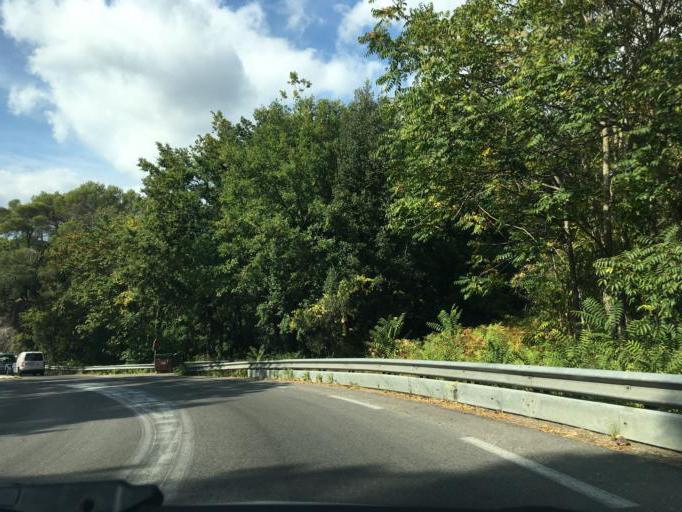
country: FR
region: Provence-Alpes-Cote d'Azur
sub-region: Departement du Var
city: Flayosc
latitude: 43.5432
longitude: 6.3614
